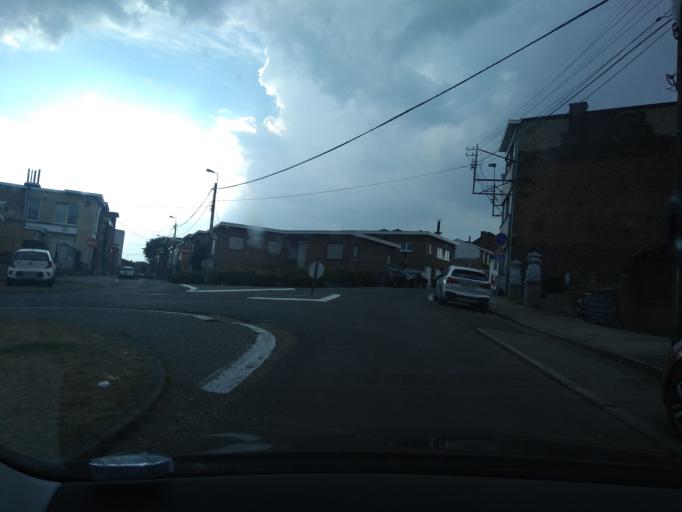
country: BE
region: Wallonia
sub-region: Province de Liege
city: Ans
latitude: 50.6591
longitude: 5.5392
